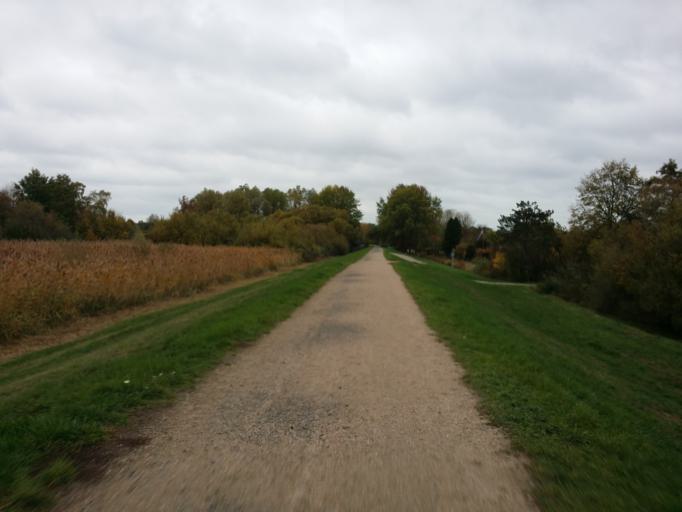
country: DE
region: Lower Saxony
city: Stuhr
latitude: 53.0515
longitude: 8.7718
